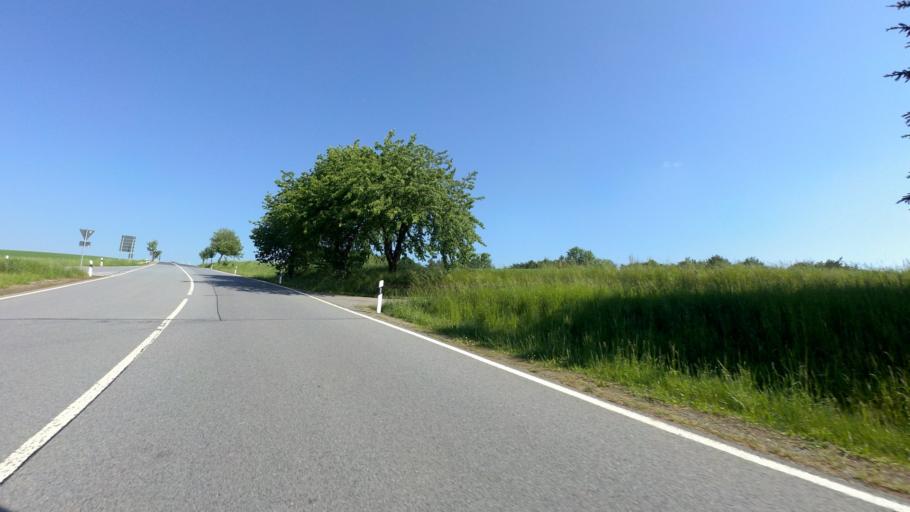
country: DE
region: Saxony
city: Hohnstein
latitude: 50.9975
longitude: 14.0805
